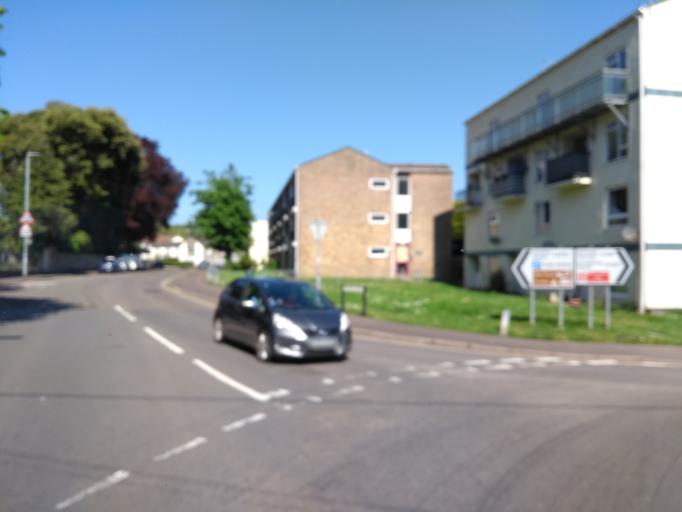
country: GB
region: England
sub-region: Somerset
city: Chard
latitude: 50.8697
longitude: -2.9631
